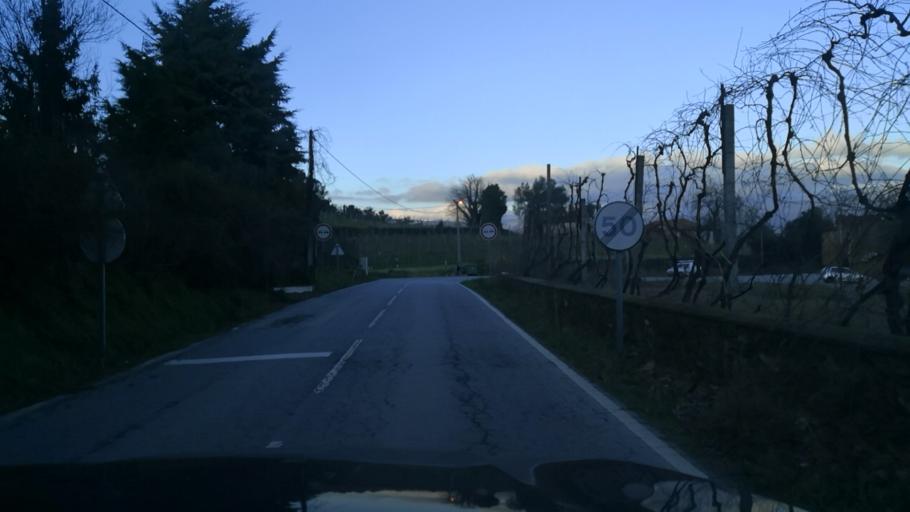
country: PT
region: Vila Real
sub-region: Mondim de Basto
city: Mondim de Basto
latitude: 41.4652
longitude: -7.9556
